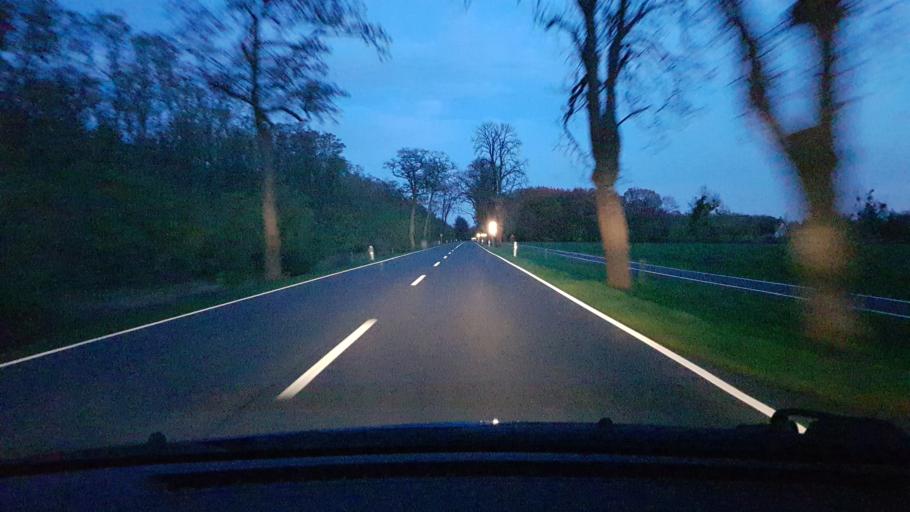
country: DE
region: Saxony-Anhalt
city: Rodleben
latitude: 51.9177
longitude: 12.1771
